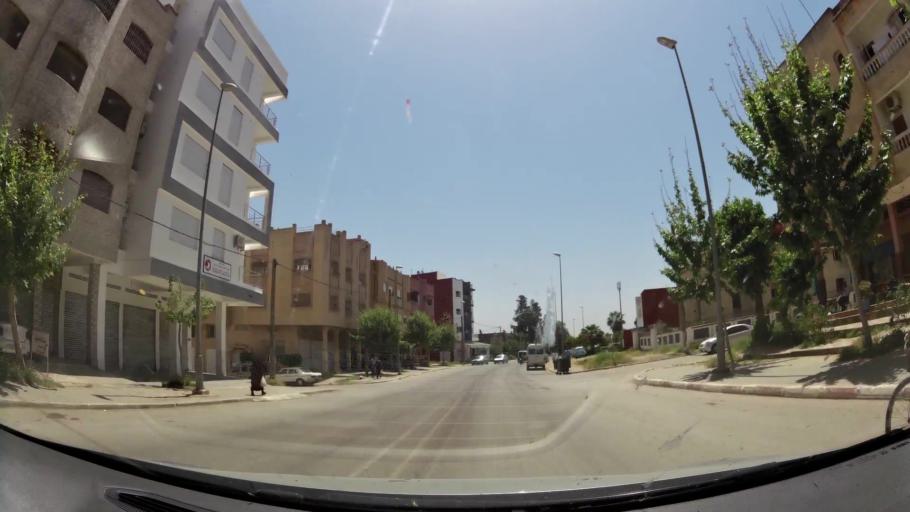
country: MA
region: Rabat-Sale-Zemmour-Zaer
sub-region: Khemisset
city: Khemisset
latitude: 33.8304
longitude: -6.0617
